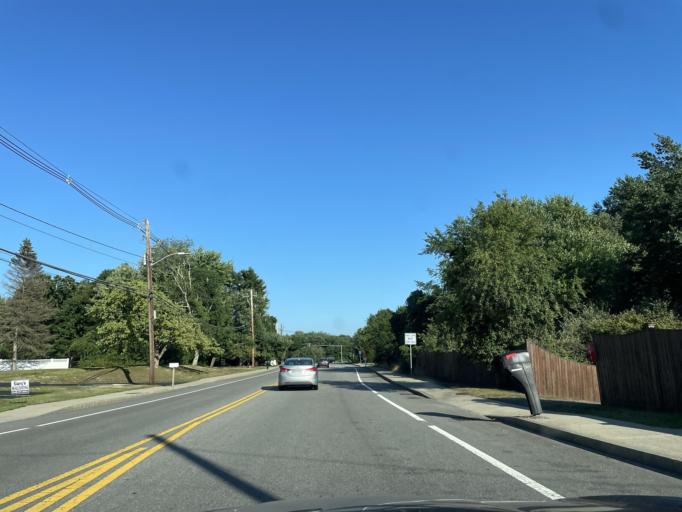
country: US
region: Massachusetts
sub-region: Bristol County
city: Mansfield Center
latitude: 42.0302
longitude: -71.1842
